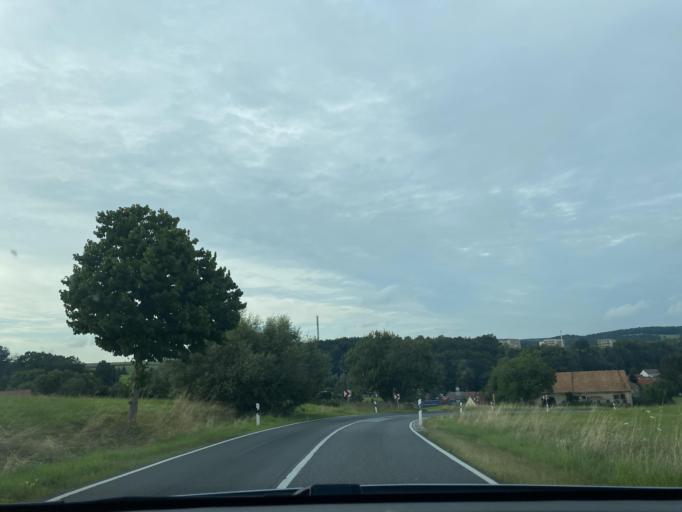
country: DE
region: Saxony
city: Bernstadt
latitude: 51.0431
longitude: 14.8198
